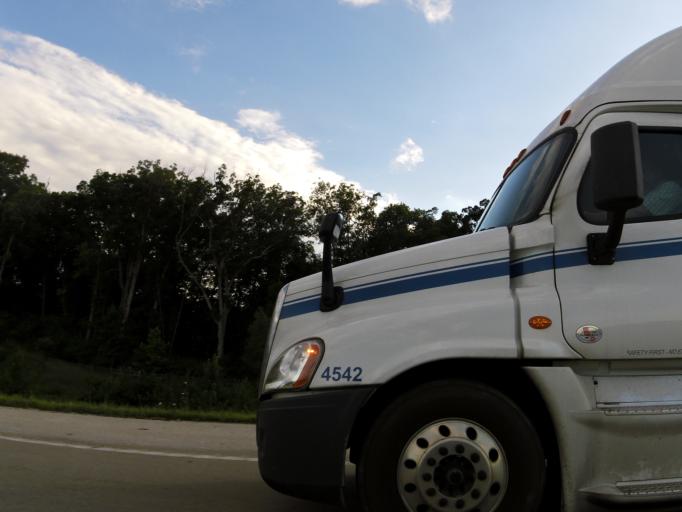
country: US
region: Missouri
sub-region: Saint Charles County
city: Dardenne Prairie
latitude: 38.7285
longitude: -90.7341
